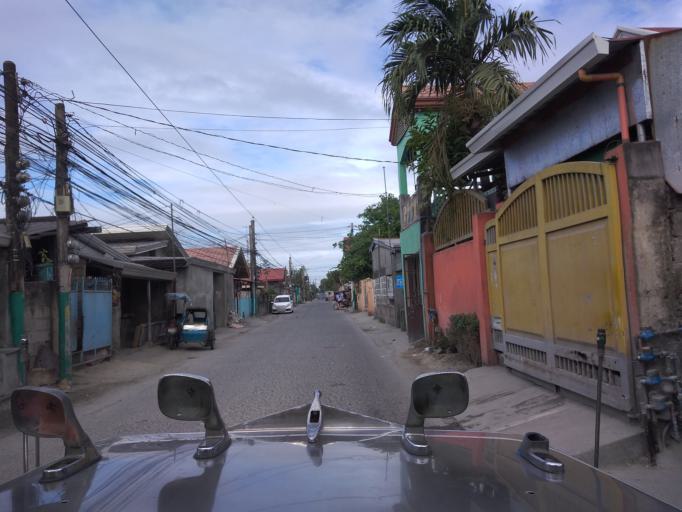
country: PH
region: Central Luzon
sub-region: Province of Pampanga
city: Mexico
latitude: 15.0677
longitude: 120.7168
